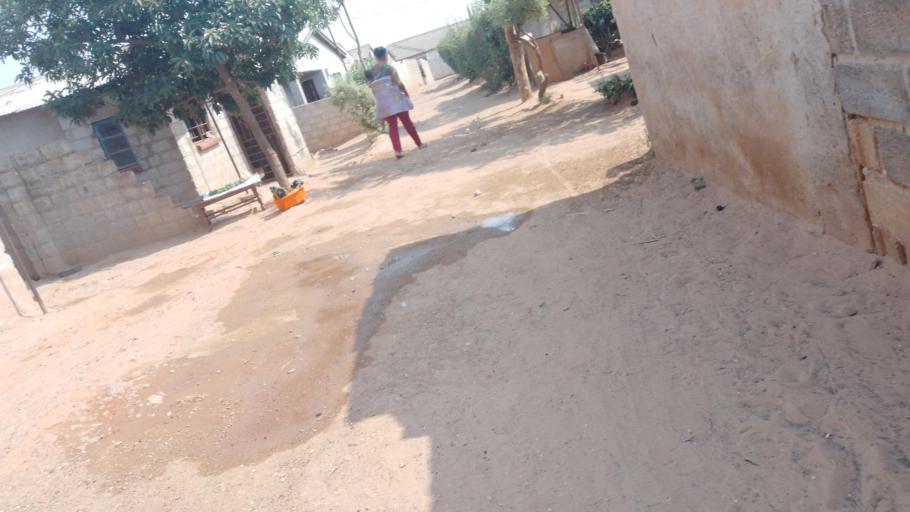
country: ZM
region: Lusaka
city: Lusaka
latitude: -15.4015
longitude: 28.3671
